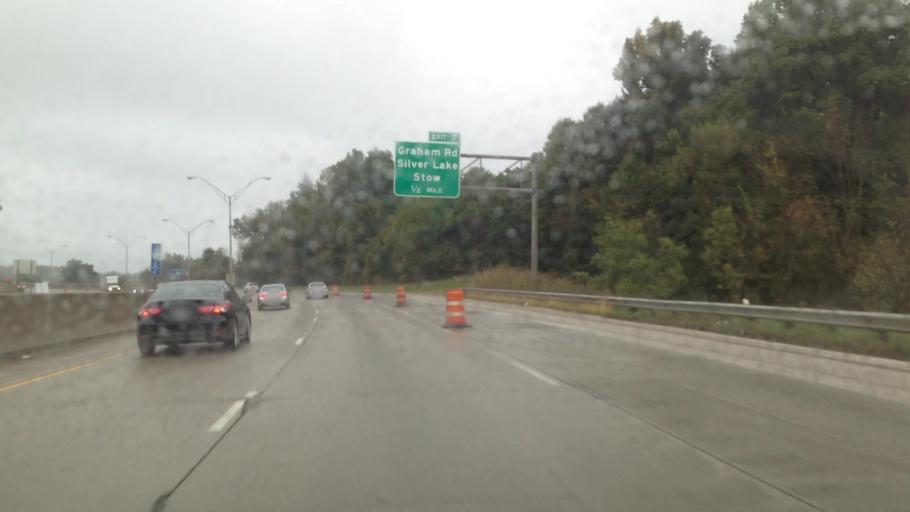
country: US
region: Ohio
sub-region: Summit County
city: Silver Lake
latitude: 41.1712
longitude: -81.4797
